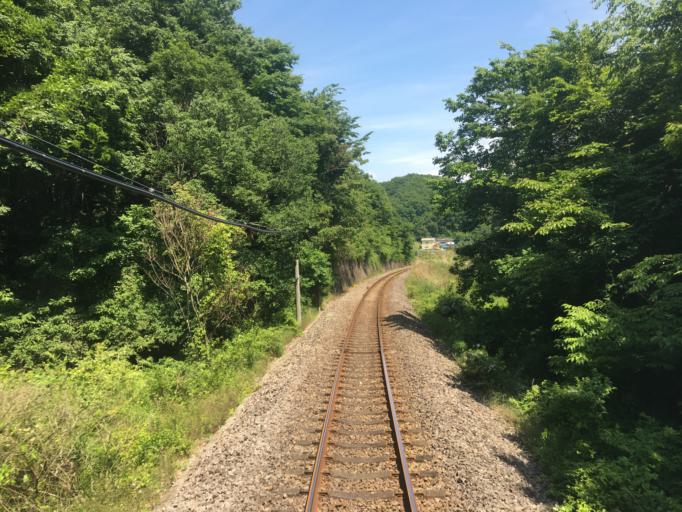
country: JP
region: Saitama
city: Yorii
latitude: 36.0854
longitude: 139.2119
